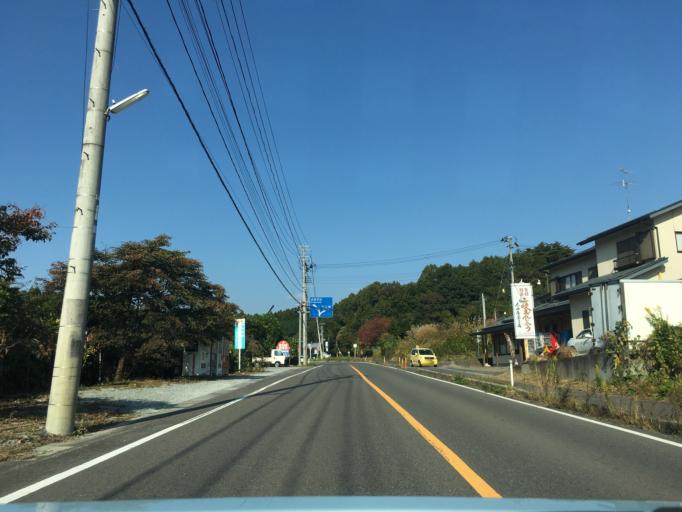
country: JP
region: Fukushima
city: Sukagawa
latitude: 37.2791
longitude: 140.2922
